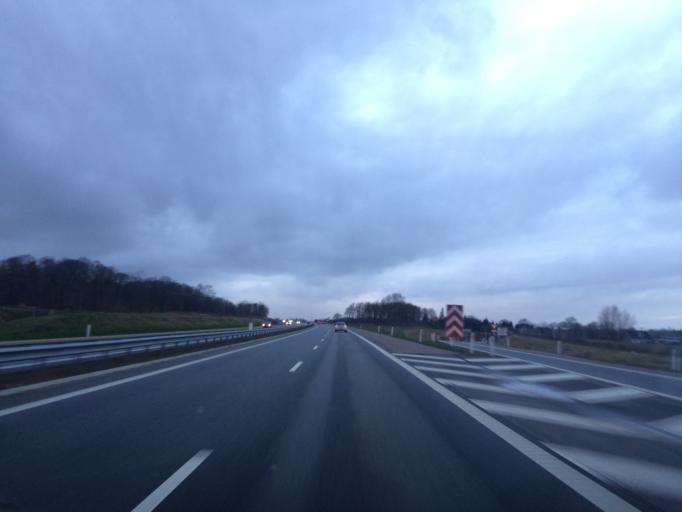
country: DK
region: South Denmark
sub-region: Sonderborg Kommune
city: Grasten
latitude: 54.9504
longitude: 9.6416
